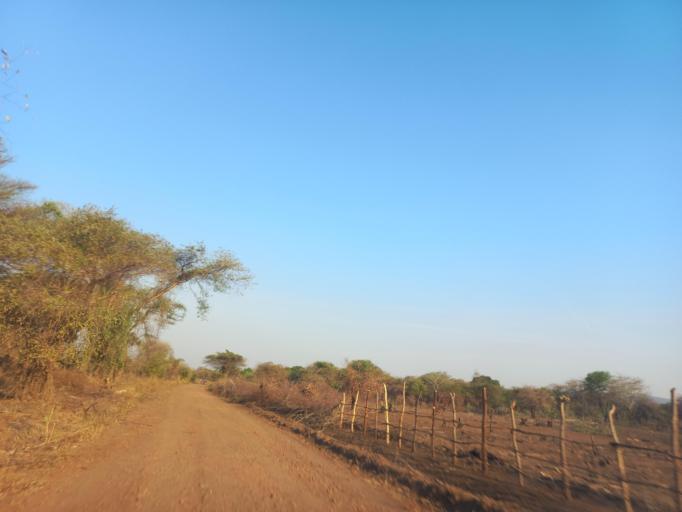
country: ZM
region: Lusaka
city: Luangwa
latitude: -15.4296
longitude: 30.3389
